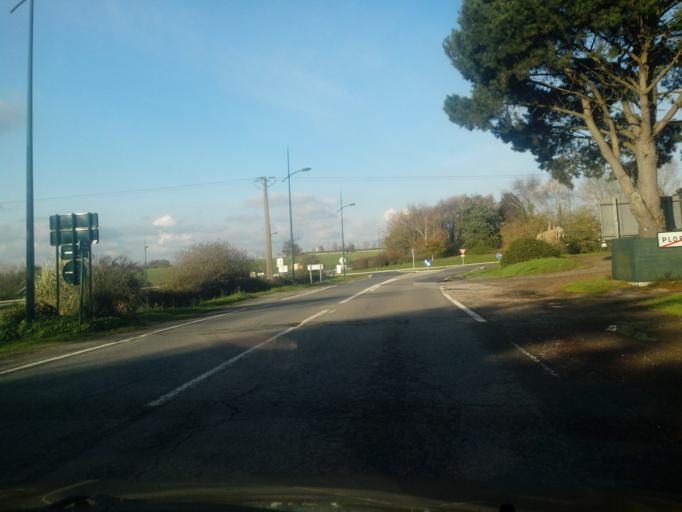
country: FR
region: Brittany
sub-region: Departement du Morbihan
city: Ploermel
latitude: 47.9418
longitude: -2.3981
